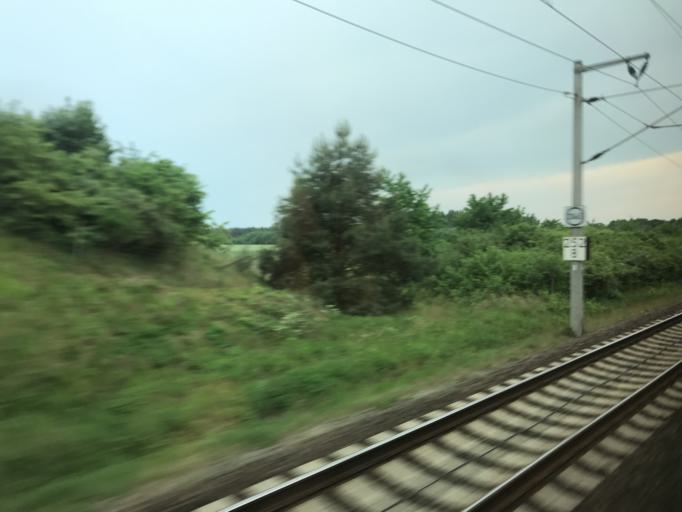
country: DE
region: Saxony-Anhalt
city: Mieste
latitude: 52.4817
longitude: 11.1953
